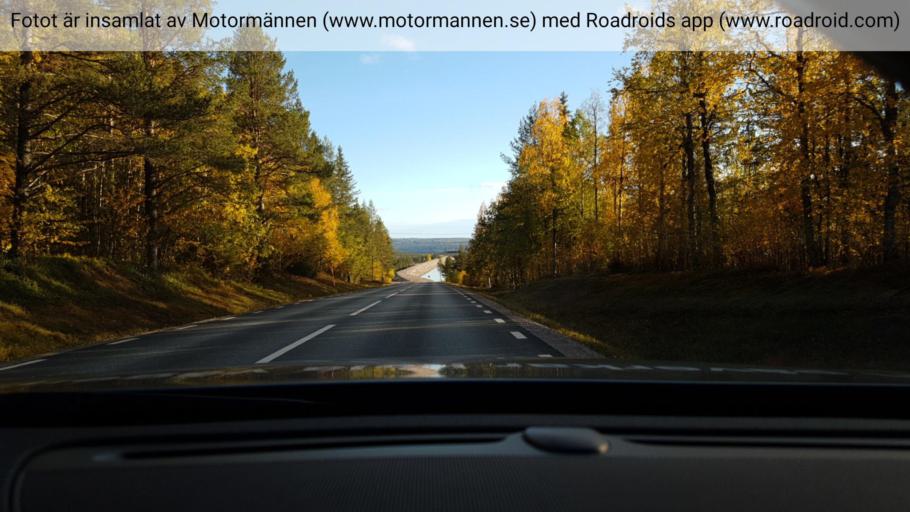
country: SE
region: Norrbotten
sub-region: Jokkmokks Kommun
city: Jokkmokk
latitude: 66.8943
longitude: 19.8276
